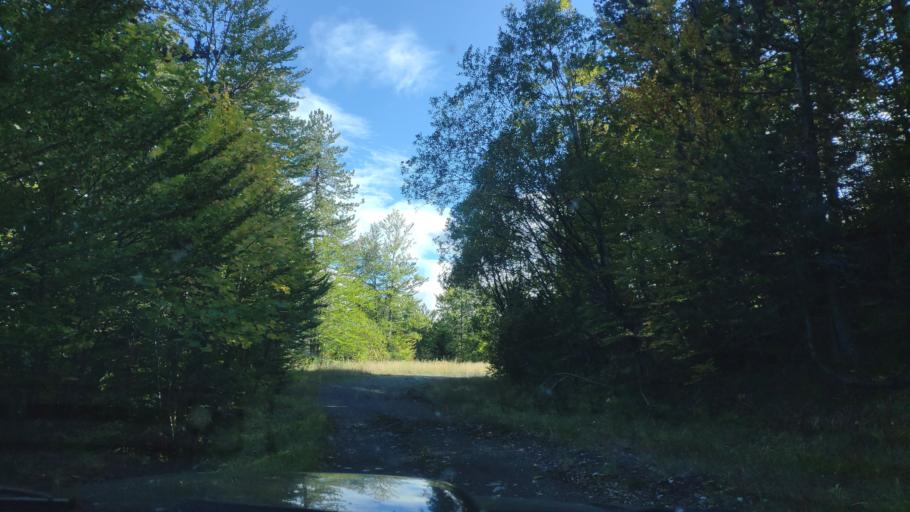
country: AL
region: Korce
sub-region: Rrethi i Devollit
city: Miras
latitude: 40.3661
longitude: 20.8980
